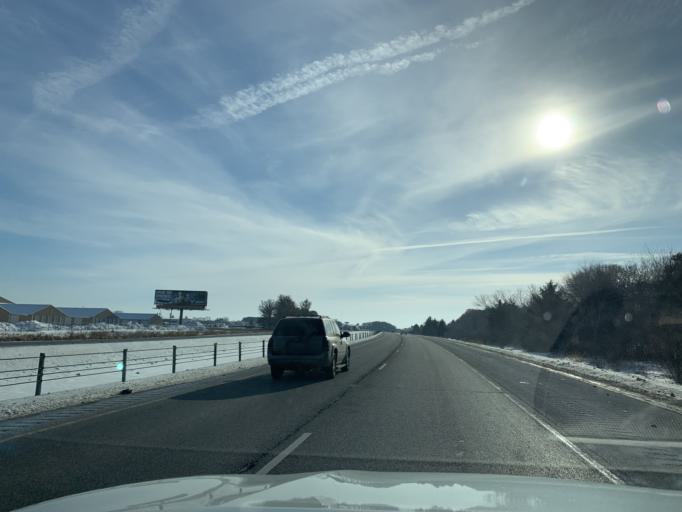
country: US
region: Minnesota
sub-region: Chisago County
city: Wyoming
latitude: 45.3305
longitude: -93.0048
